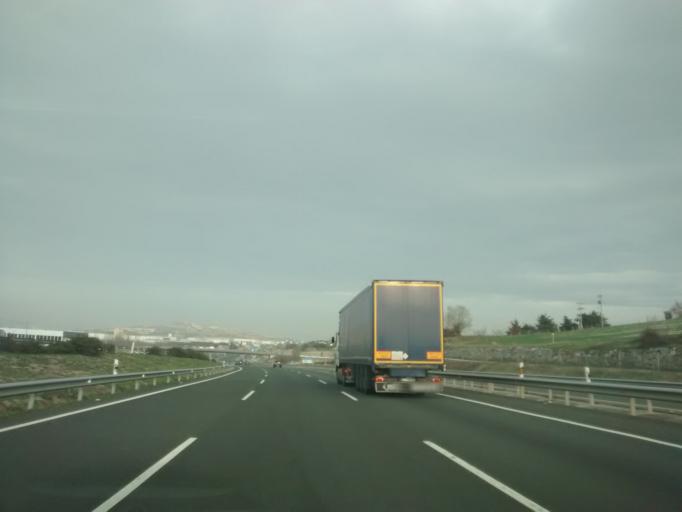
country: ES
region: Basque Country
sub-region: Provincia de Alava
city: Arminon
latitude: 42.8076
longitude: -2.8020
